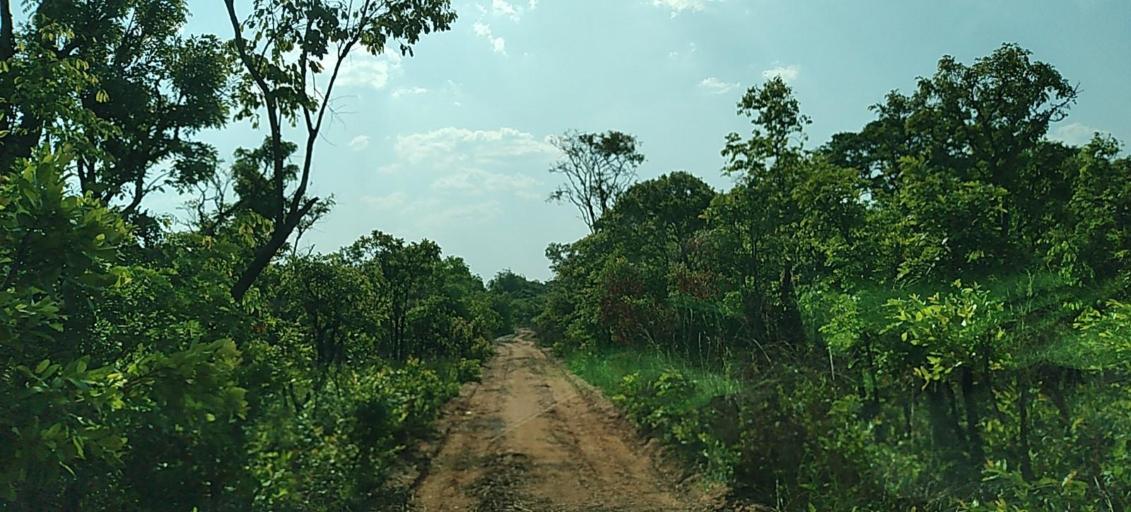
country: ZM
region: North-Western
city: Mwinilunga
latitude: -11.2978
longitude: 24.8614
